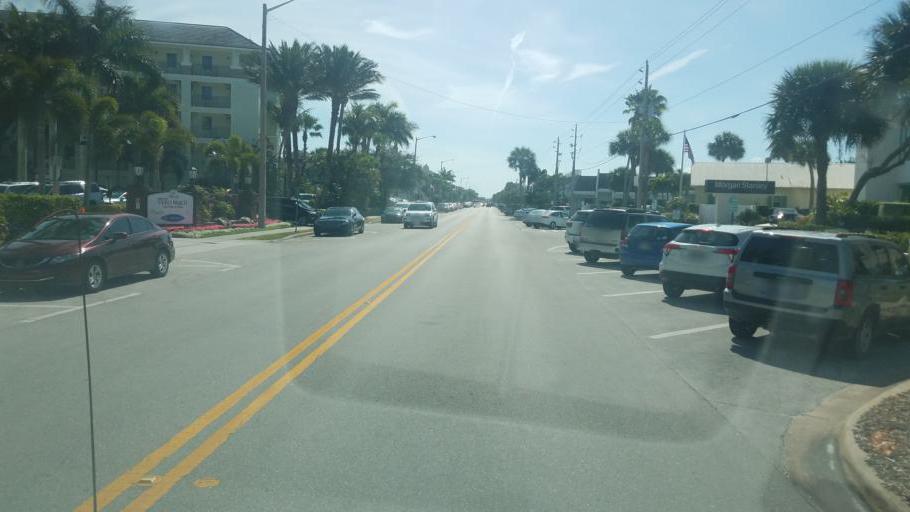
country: US
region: Florida
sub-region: Indian River County
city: Vero Beach
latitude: 27.6561
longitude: -80.3574
